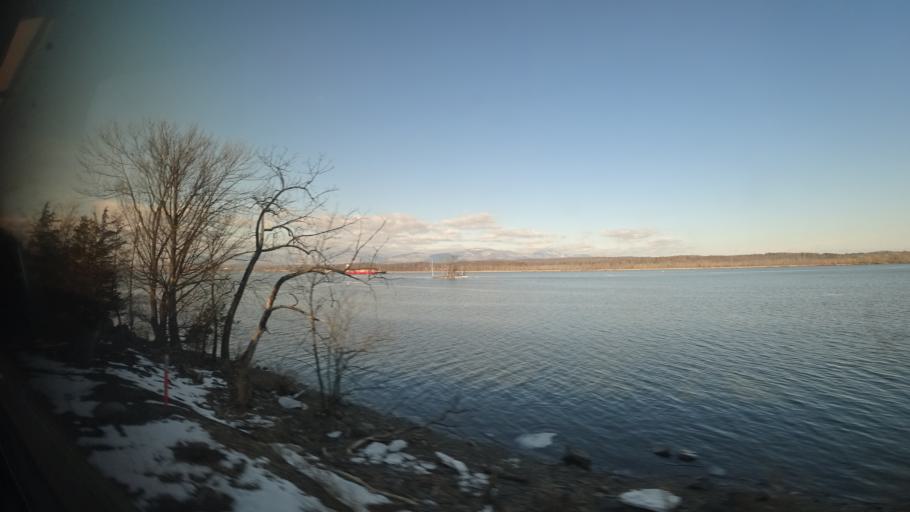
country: US
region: New York
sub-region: Greene County
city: Catskill
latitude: 42.1837
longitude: -73.8563
